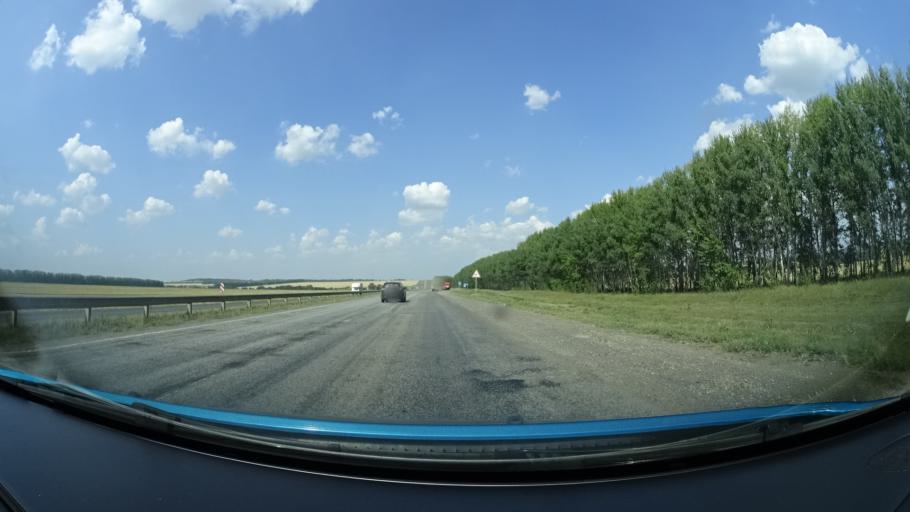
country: RU
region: Bashkortostan
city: Dmitriyevka
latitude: 54.6961
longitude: 55.2744
